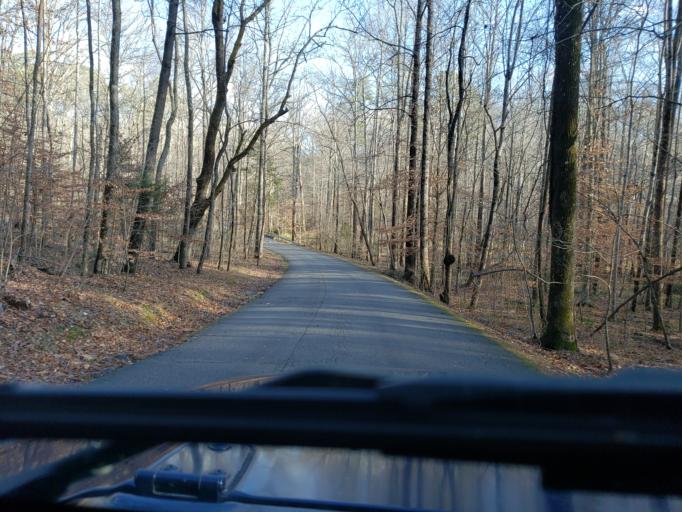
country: US
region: North Carolina
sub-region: Cleveland County
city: Kings Mountain
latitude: 35.1512
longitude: -81.3398
